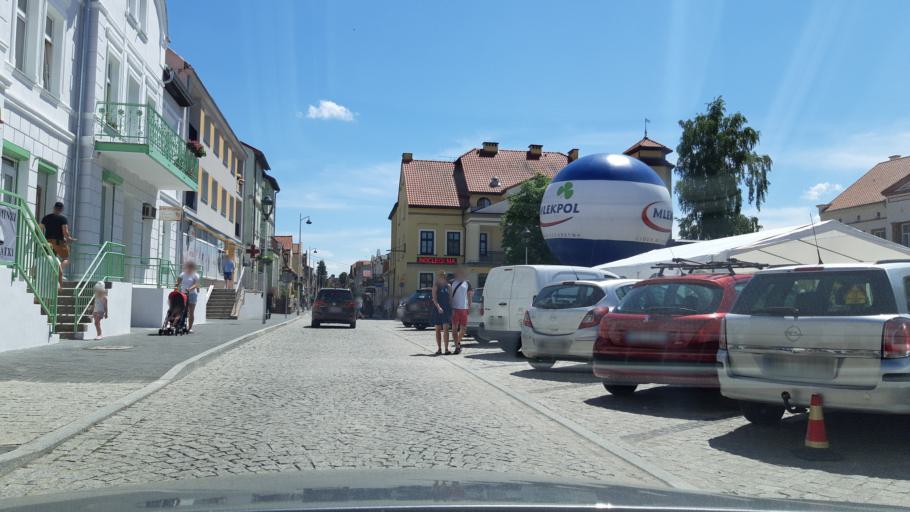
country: PL
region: Warmian-Masurian Voivodeship
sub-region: Powiat mragowski
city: Mikolajki
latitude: 53.8007
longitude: 21.5728
